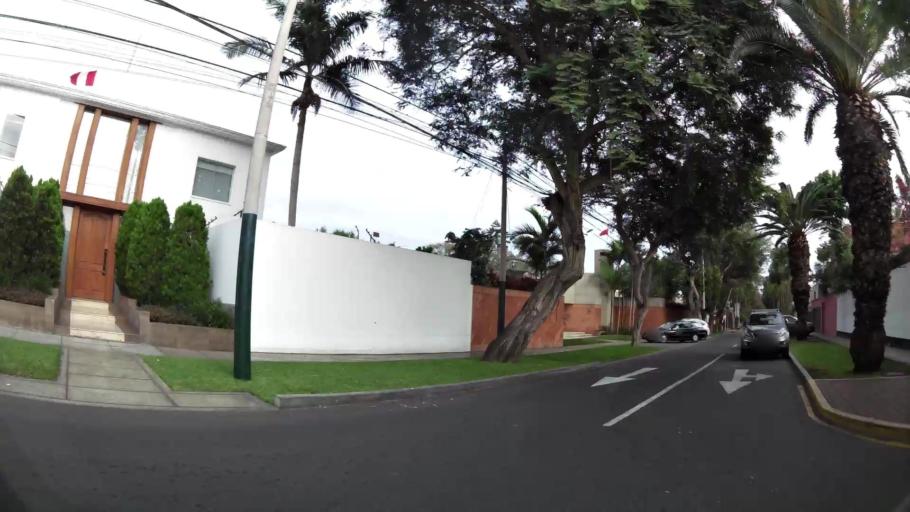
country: PE
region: Lima
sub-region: Lima
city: San Isidro
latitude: -12.0989
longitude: -77.0575
